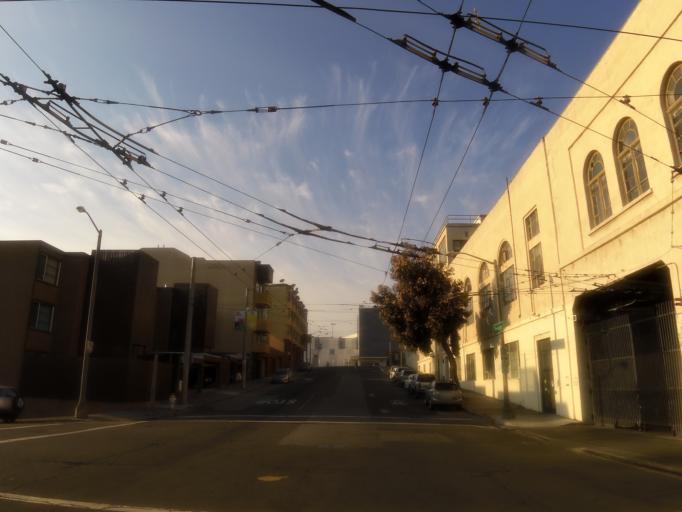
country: US
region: California
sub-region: San Francisco County
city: San Francisco
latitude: 37.7837
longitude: -122.4461
